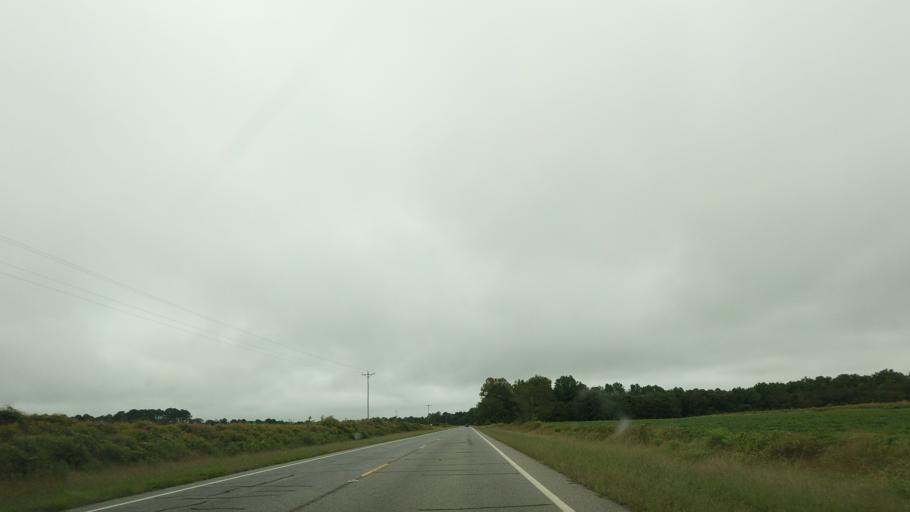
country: US
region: Georgia
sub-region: Irwin County
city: Ocilla
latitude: 31.5295
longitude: -83.2467
